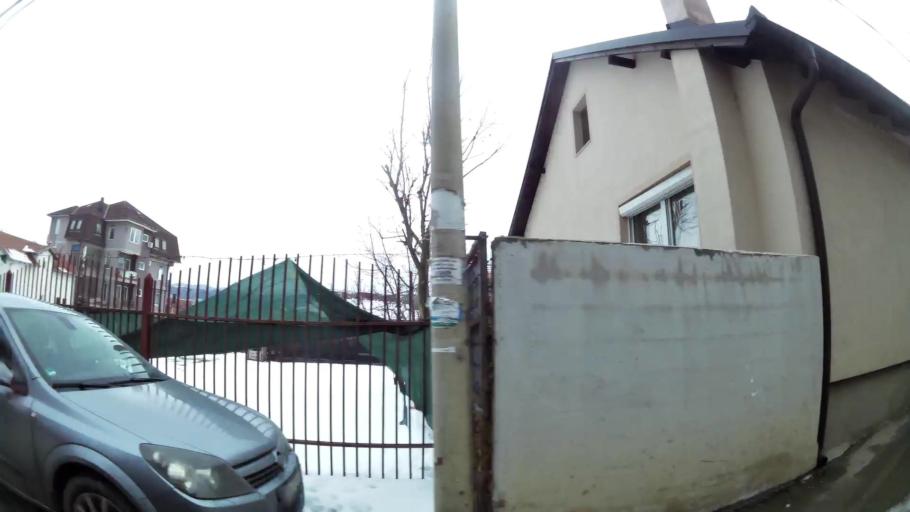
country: XK
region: Pristina
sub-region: Komuna e Prishtines
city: Pristina
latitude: 42.6609
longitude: 21.1821
